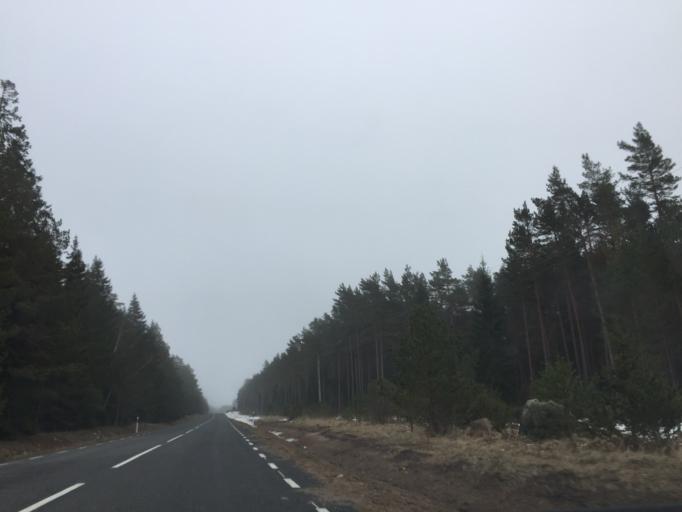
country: EE
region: Saare
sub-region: Kuressaare linn
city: Kuressaare
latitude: 58.4694
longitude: 22.0335
